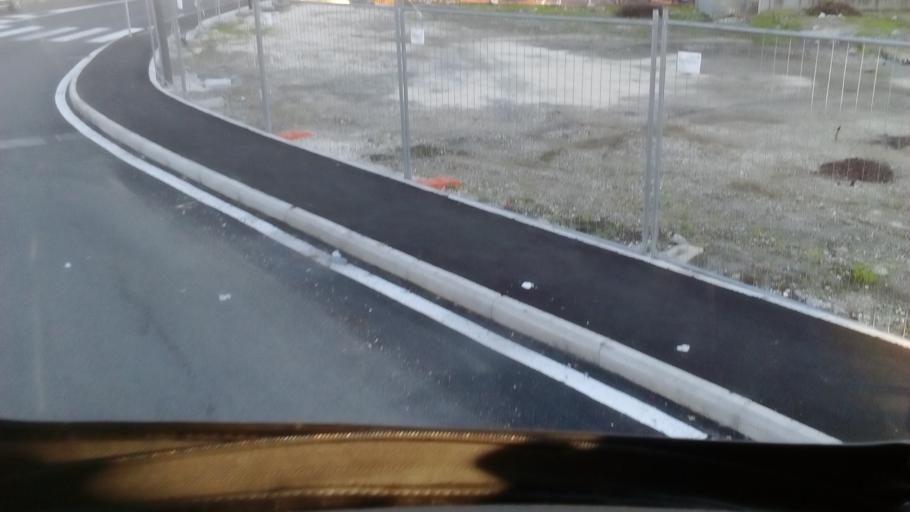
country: IT
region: Latium
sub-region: Citta metropolitana di Roma Capitale
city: Albano Laziale
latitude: 41.7148
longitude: 12.6304
